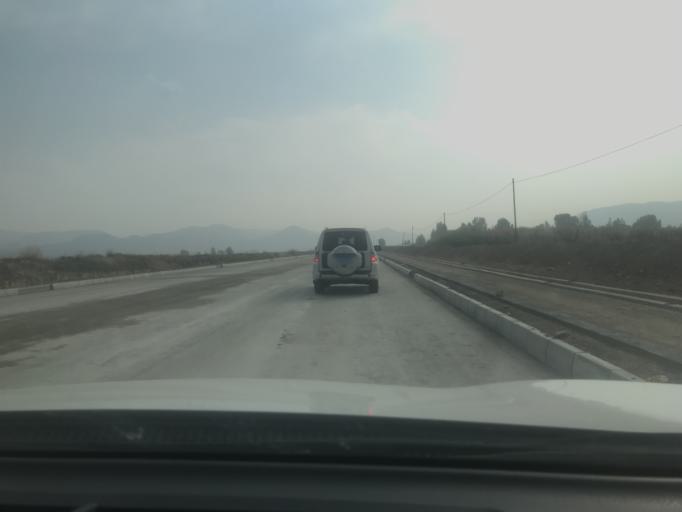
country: CN
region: Gansu Sheng
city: Gulang
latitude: 37.5048
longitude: 102.9014
